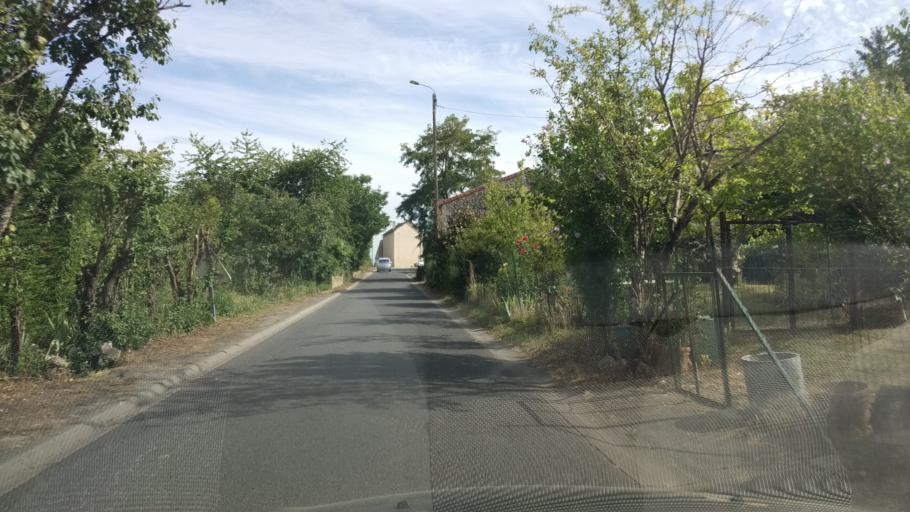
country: FR
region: Poitou-Charentes
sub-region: Departement de la Vienne
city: Chauvigny
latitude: 46.4801
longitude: 0.6481
